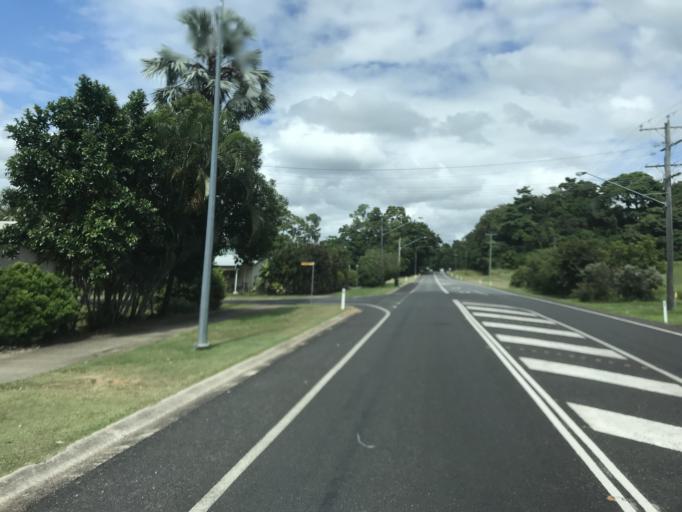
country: AU
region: Queensland
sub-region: Cassowary Coast
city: Innisfail
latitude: -17.8711
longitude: 146.1025
